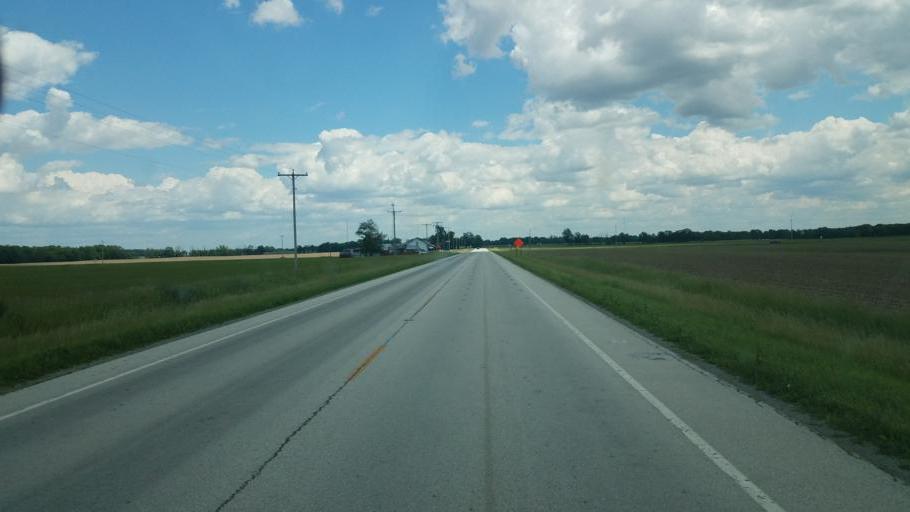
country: US
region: Ohio
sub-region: Wyandot County
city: Upper Sandusky
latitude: 40.8407
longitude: -83.1353
